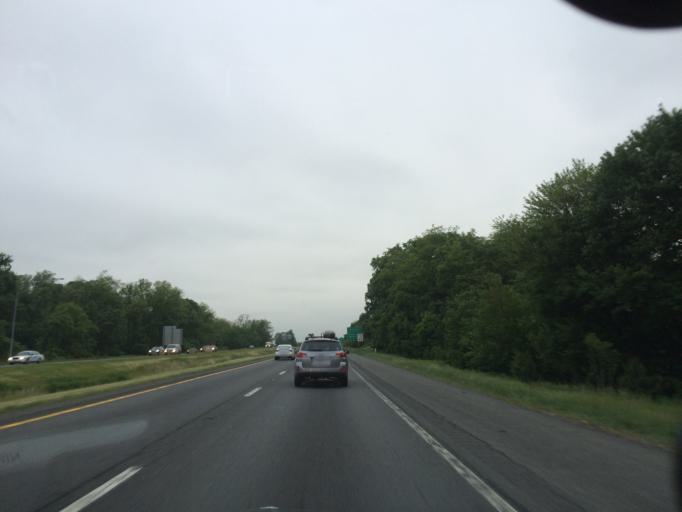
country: US
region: Maryland
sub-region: Washington County
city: Halfway
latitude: 39.6066
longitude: -77.7621
